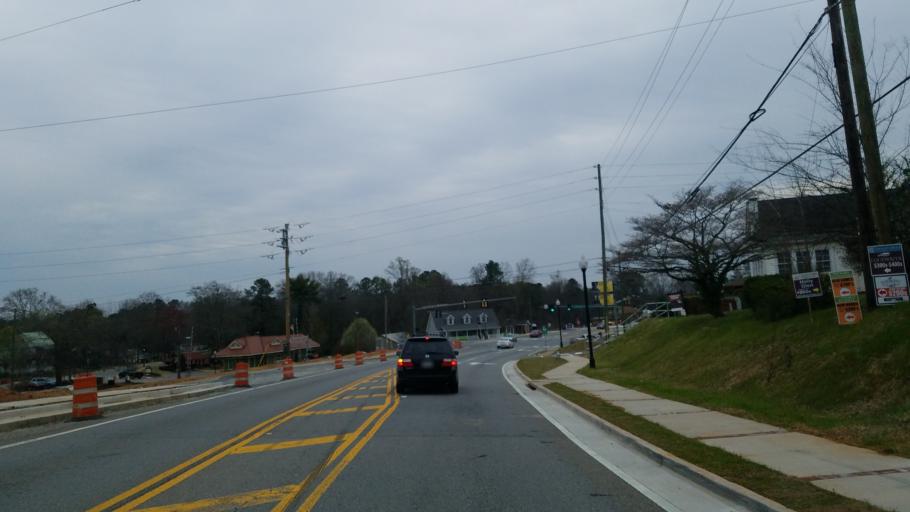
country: US
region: Georgia
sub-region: Cherokee County
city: Holly Springs
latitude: 34.1745
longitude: -84.5013
